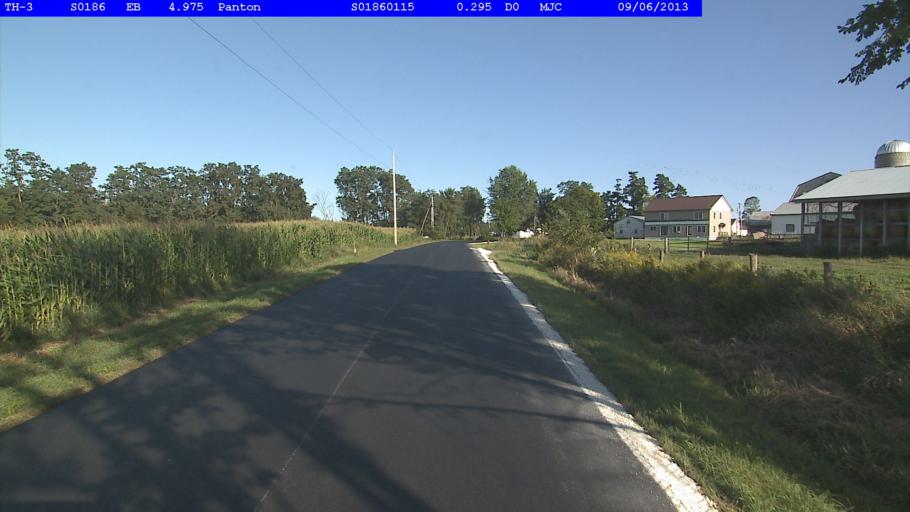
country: US
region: Vermont
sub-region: Addison County
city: Vergennes
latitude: 44.1605
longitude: -73.2884
